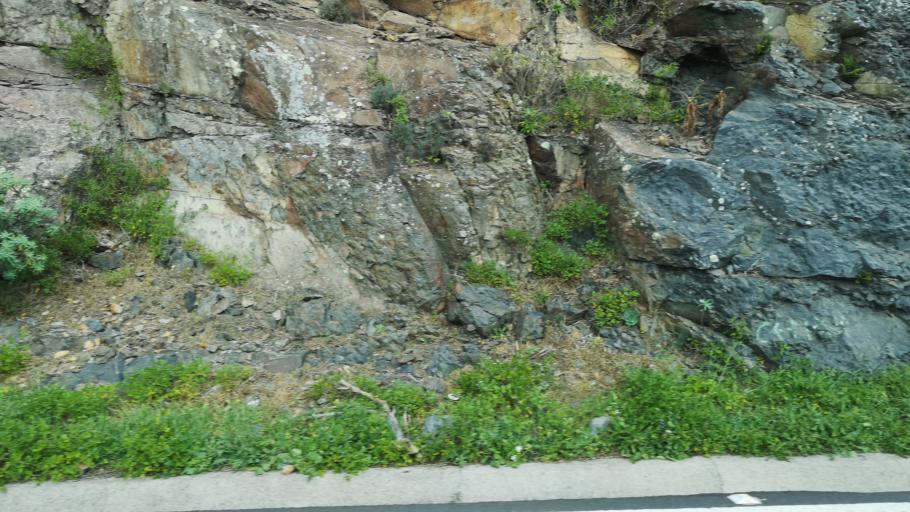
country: ES
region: Canary Islands
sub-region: Provincia de Santa Cruz de Tenerife
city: Alajero
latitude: 28.1010
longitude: -17.2081
